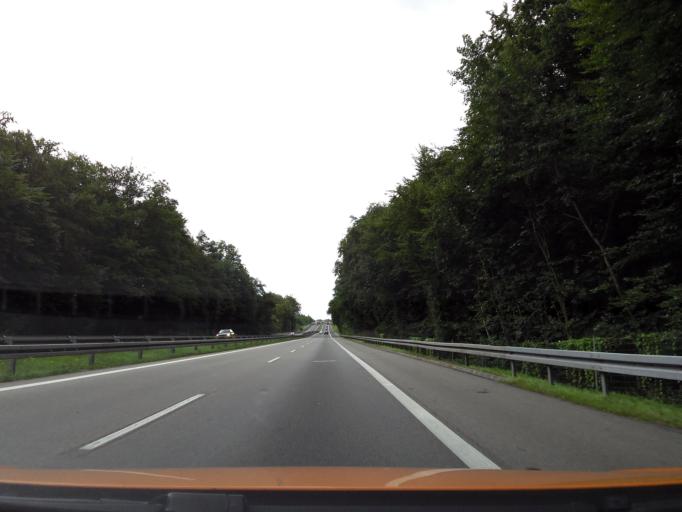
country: PL
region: West Pomeranian Voivodeship
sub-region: Szczecin
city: Szczecin
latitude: 53.3518
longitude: 14.6029
